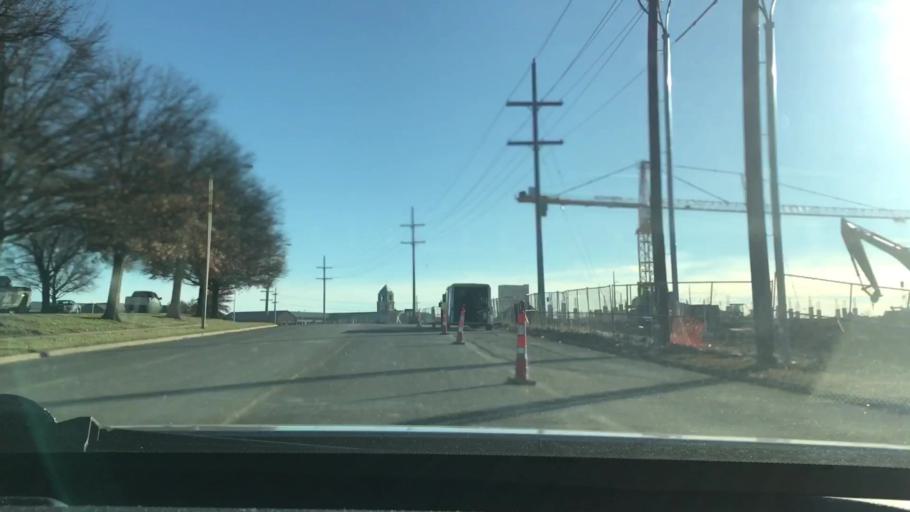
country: US
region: Kansas
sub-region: Johnson County
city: Leawood
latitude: 38.9242
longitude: -94.6583
